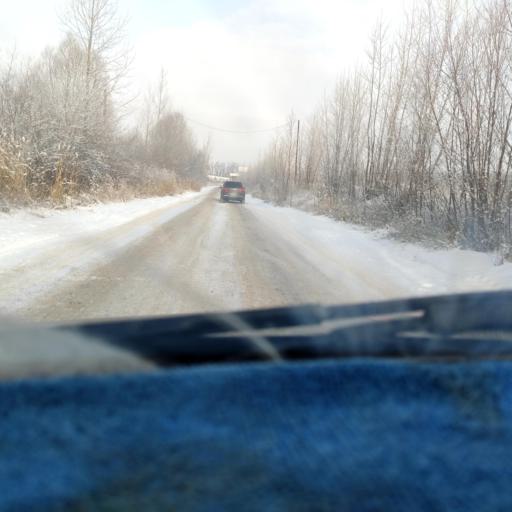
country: RU
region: Bashkortostan
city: Avdon
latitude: 54.6716
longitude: 55.8155
